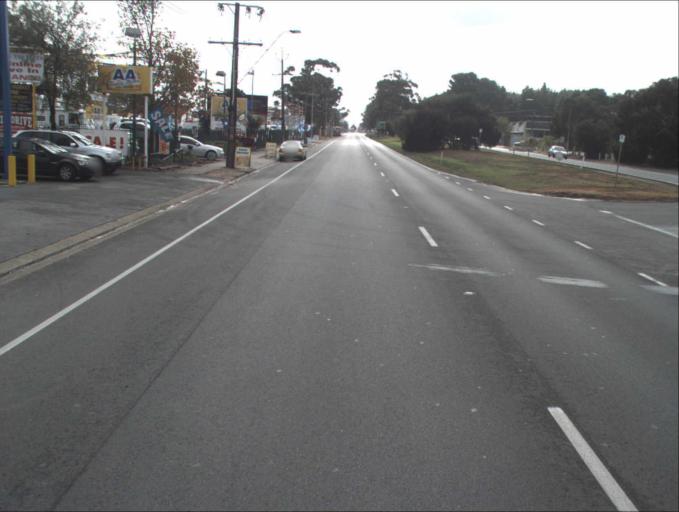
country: AU
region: South Australia
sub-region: Port Adelaide Enfield
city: Enfield
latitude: -34.8451
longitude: 138.6023
